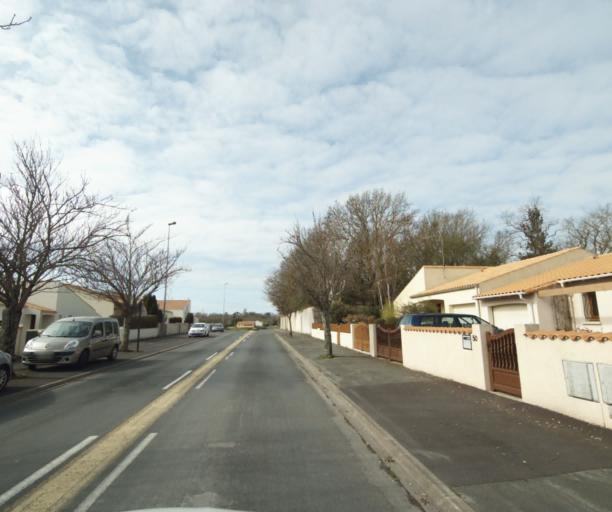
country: FR
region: Poitou-Charentes
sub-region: Departement de la Charente-Maritime
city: Lagord
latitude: 46.1820
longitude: -1.1653
